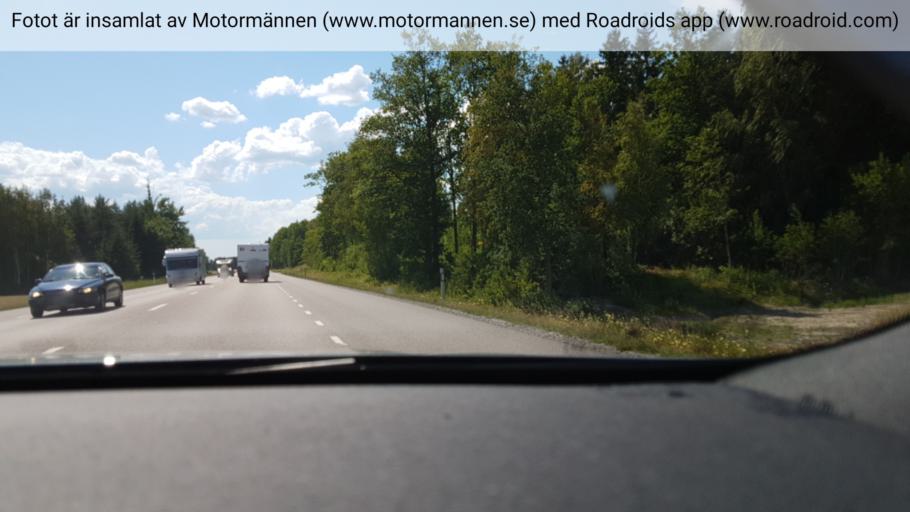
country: SE
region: Vaestra Goetaland
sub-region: Grastorps Kommun
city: Graestorp
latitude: 58.3229
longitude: 12.5761
